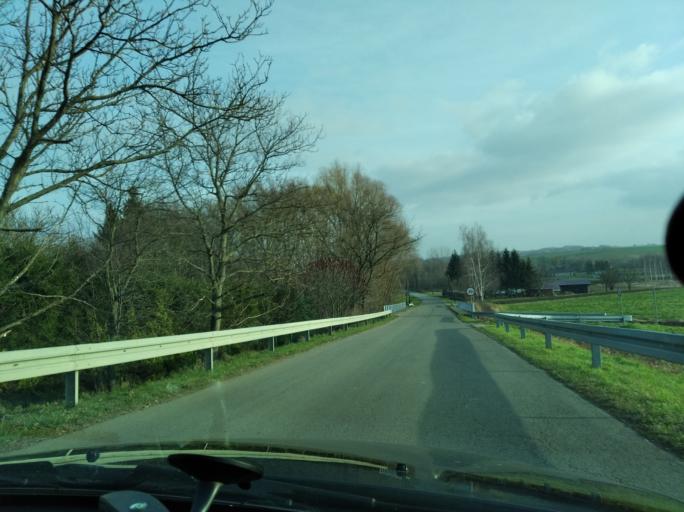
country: PL
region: Subcarpathian Voivodeship
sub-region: Powiat przeworski
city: Siedleczka
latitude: 49.9553
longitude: 22.3912
